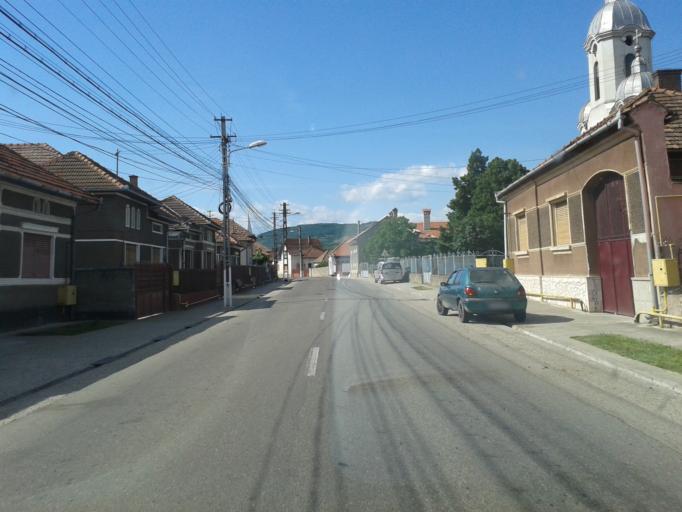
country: RO
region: Hunedoara
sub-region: Comuna Geoagiu
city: Geoagiu
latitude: 45.9117
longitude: 23.2062
